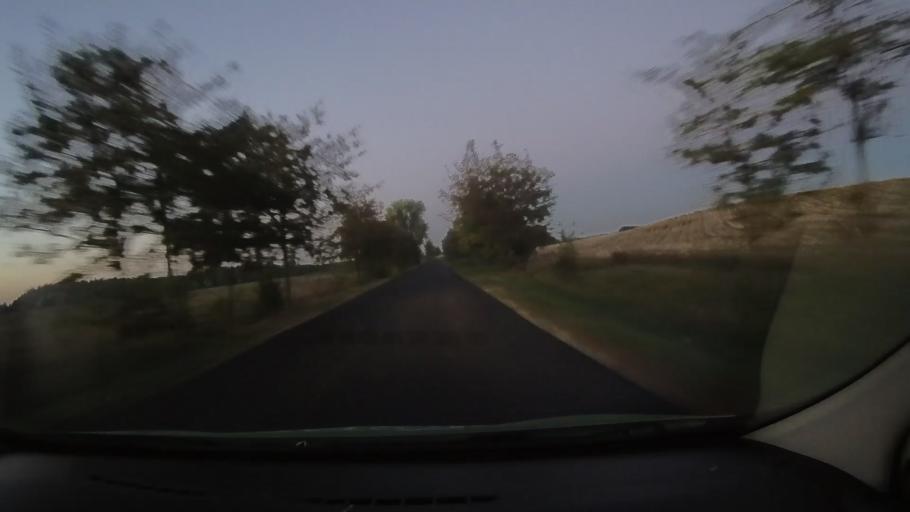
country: RO
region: Bihor
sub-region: Comuna Simian
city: Simian
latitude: 47.5054
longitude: 22.0938
